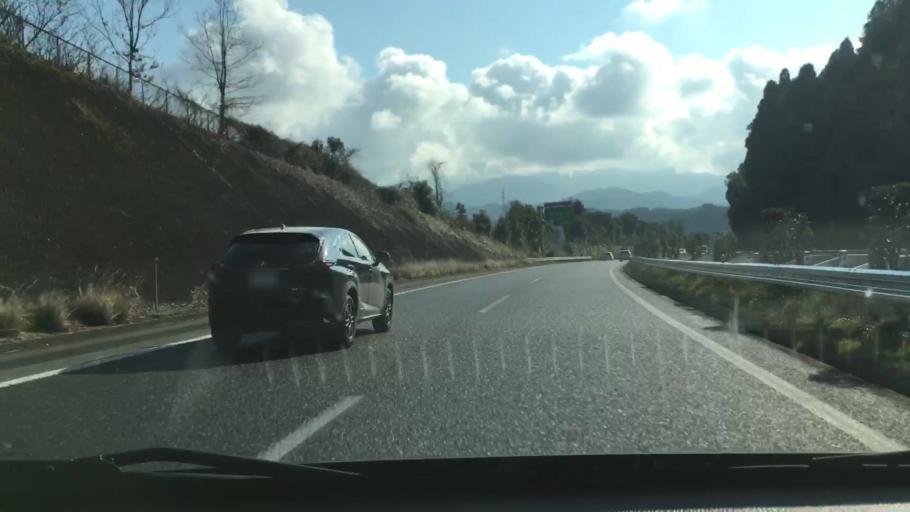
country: JP
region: Kumamoto
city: Matsubase
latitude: 32.5865
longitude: 130.7165
